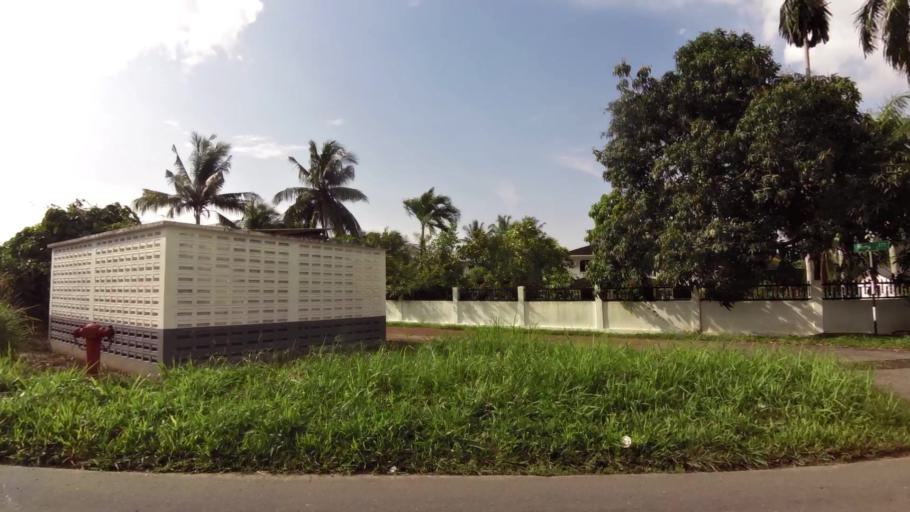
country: BN
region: Brunei and Muara
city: Bandar Seri Begawan
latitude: 4.9574
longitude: 114.9695
